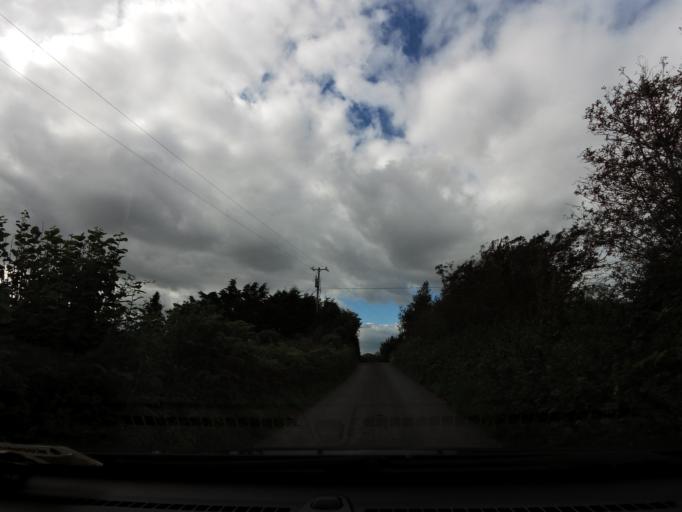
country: IE
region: Connaught
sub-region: County Galway
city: Moycullen
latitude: 53.3337
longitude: -9.1516
